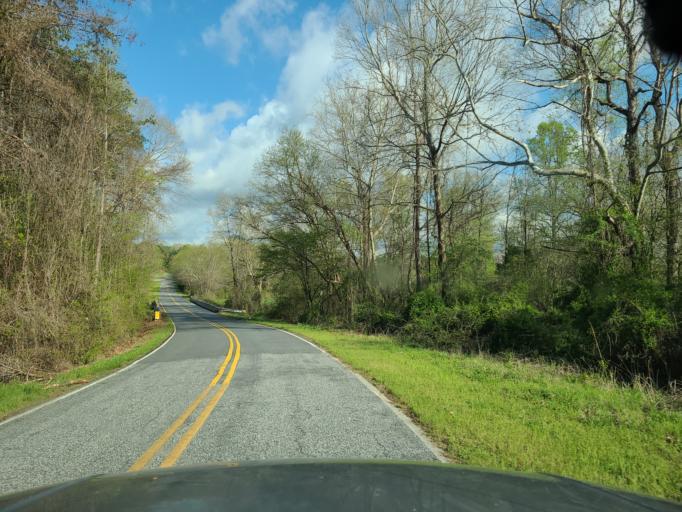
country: US
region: North Carolina
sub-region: Rutherford County
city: Forest City
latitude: 35.4198
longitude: -81.8206
